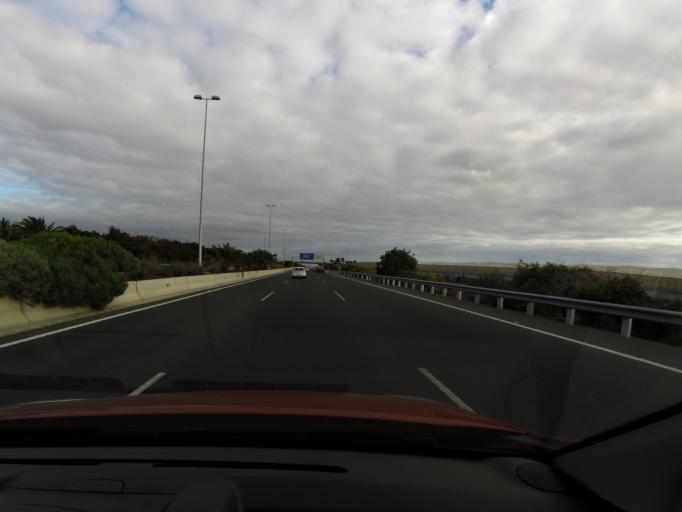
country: ES
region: Canary Islands
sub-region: Provincia de Las Palmas
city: Cruce de Arinaga
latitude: 27.8372
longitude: -15.4412
